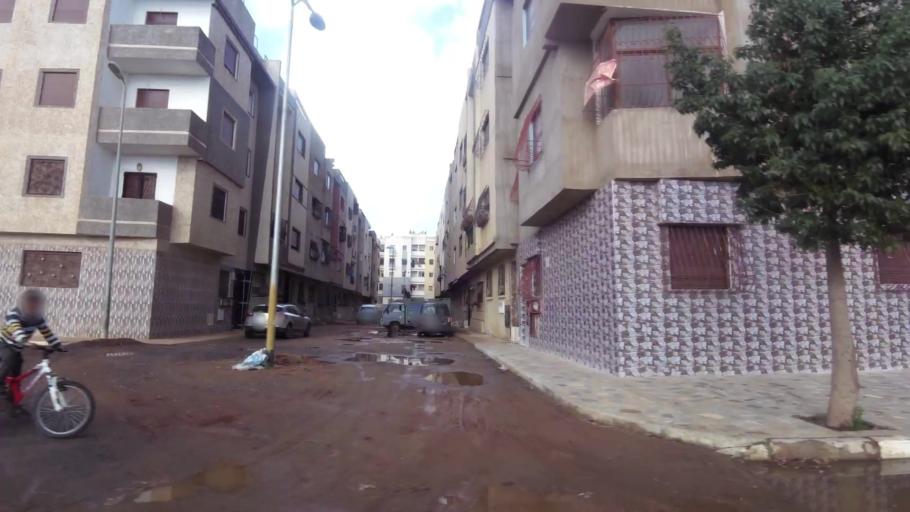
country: MA
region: Grand Casablanca
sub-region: Nouaceur
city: Bouskoura
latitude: 33.5370
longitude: -7.7018
